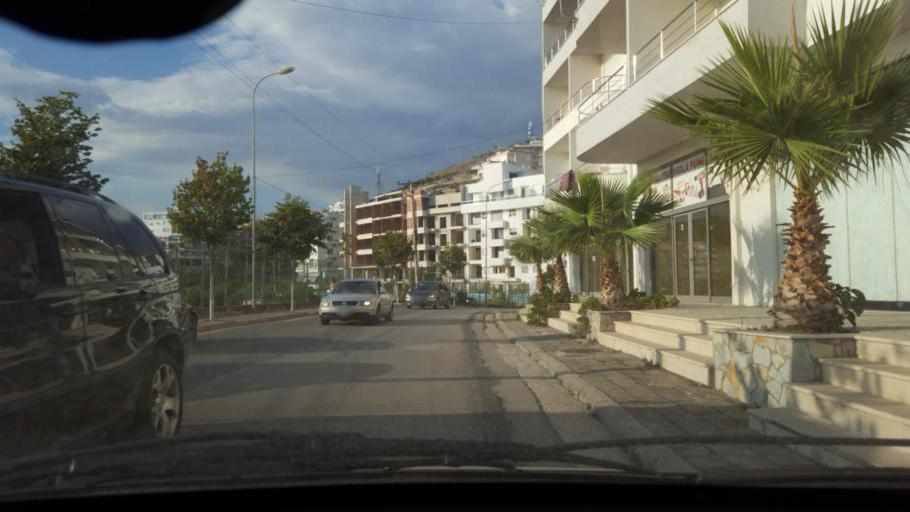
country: AL
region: Vlore
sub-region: Rrethi i Sarandes
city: Sarande
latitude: 39.8574
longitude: 20.0206
